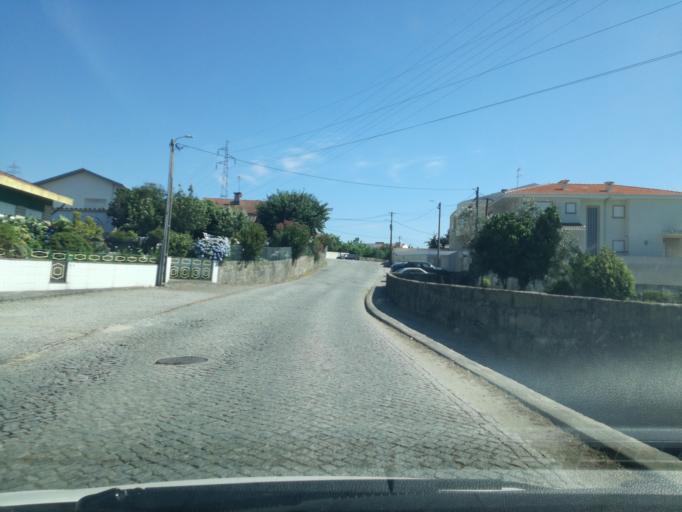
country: PT
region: Porto
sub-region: Maia
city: Anta
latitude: 41.2701
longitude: -8.6326
